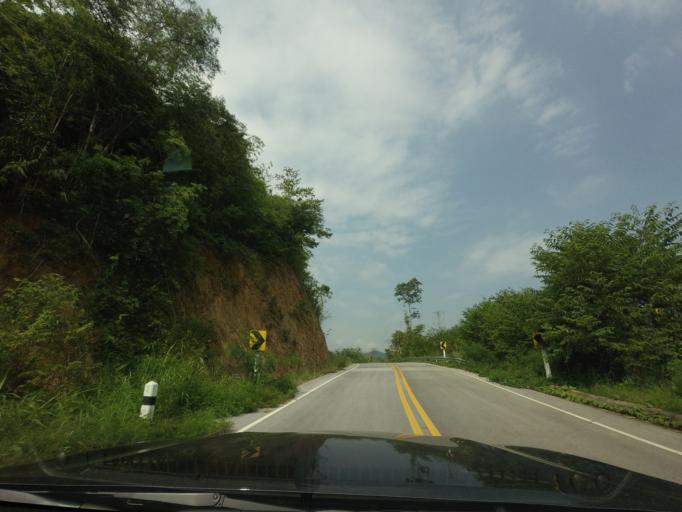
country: LA
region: Xiagnabouli
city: Muang Kenthao
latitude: 17.7736
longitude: 101.5306
